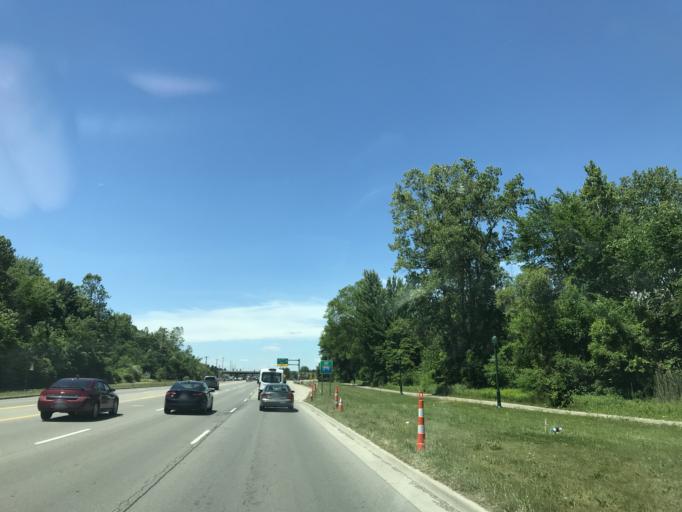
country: US
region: Michigan
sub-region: Wayne County
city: Westland
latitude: 42.3234
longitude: -83.4363
